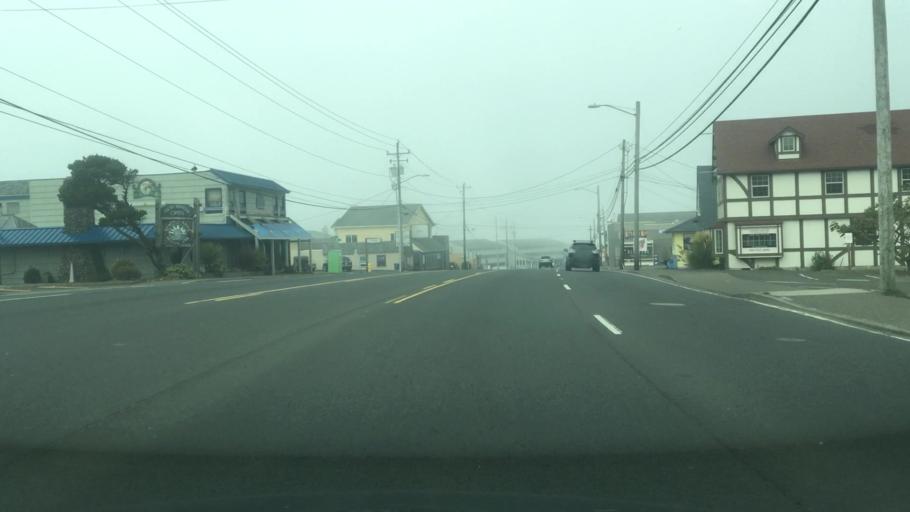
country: US
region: Oregon
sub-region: Lincoln County
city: Lincoln City
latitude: 44.9636
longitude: -124.0175
